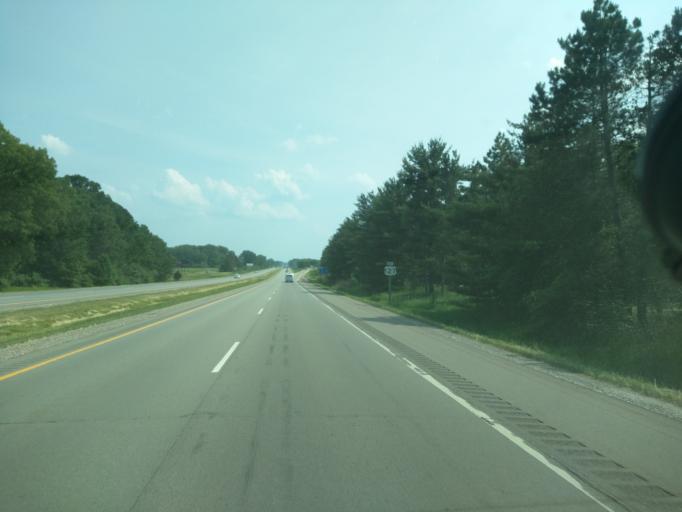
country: US
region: Michigan
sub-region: Ingham County
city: Leslie
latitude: 42.3721
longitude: -84.4290
